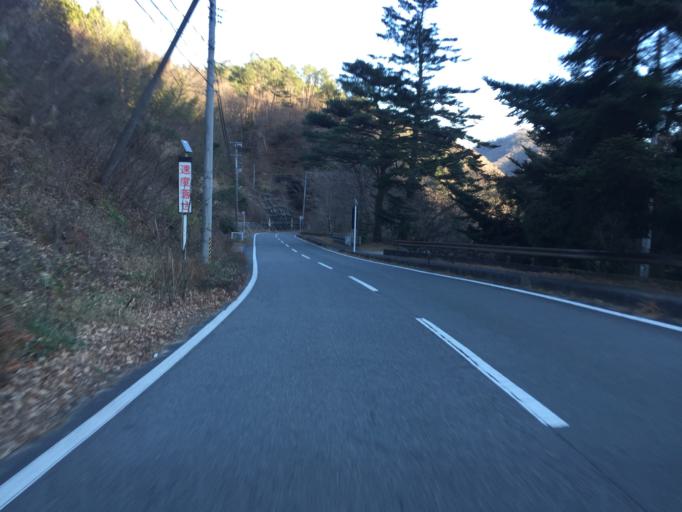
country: JP
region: Fukushima
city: Iwaki
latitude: 37.1832
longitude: 140.8188
